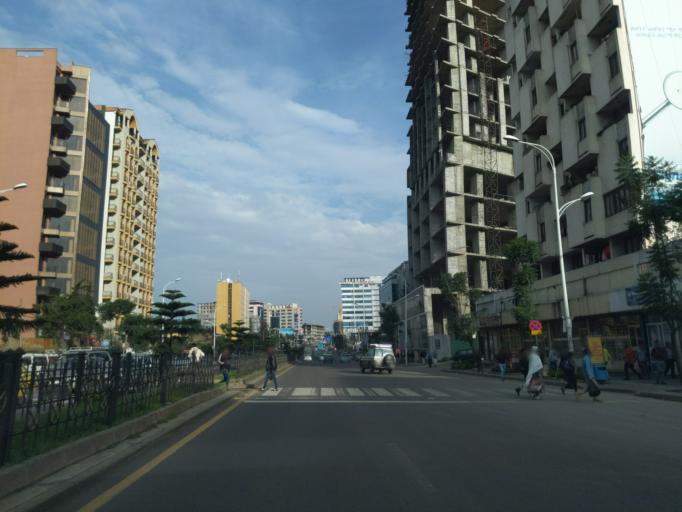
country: ET
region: Adis Abeba
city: Addis Ababa
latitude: 9.0090
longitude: 38.7645
